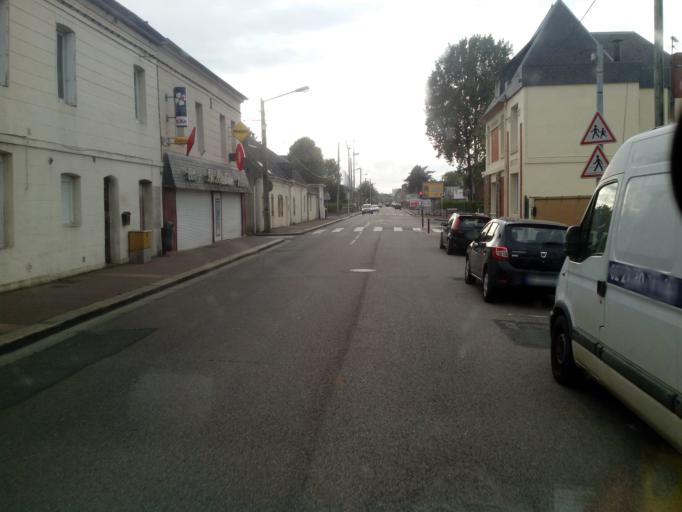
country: FR
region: Haute-Normandie
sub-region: Departement de la Seine-Maritime
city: Fecamp
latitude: 49.7522
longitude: 0.3954
